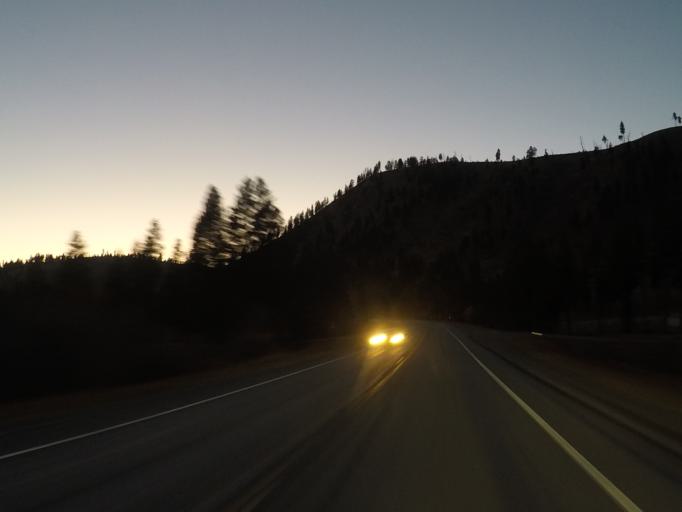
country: US
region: Montana
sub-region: Missoula County
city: Seeley Lake
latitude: 47.0245
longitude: -113.3039
